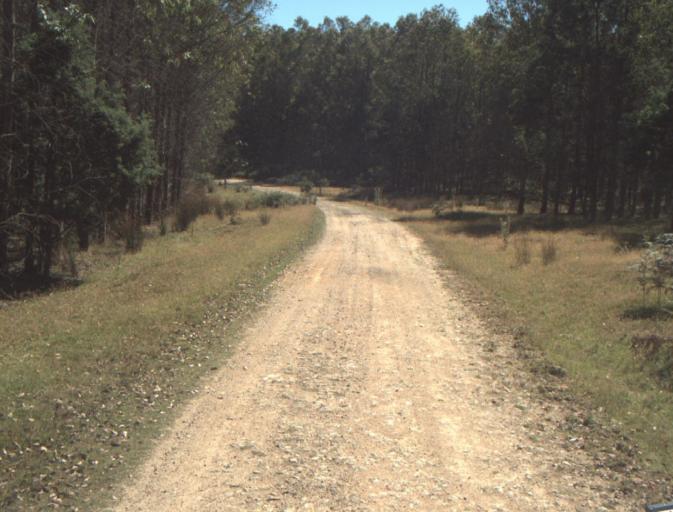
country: AU
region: Tasmania
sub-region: Dorset
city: Scottsdale
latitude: -41.2627
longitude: 147.3506
